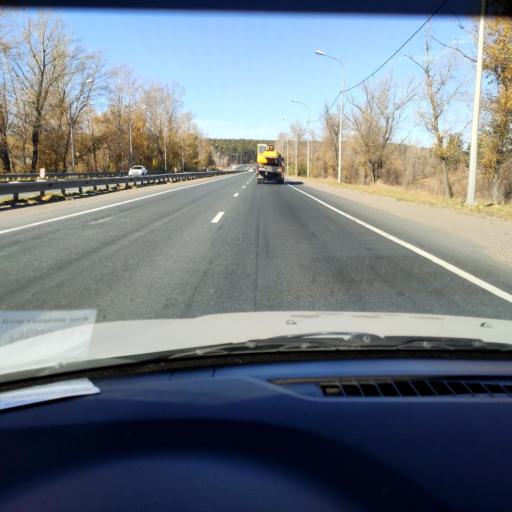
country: RU
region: Samara
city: Zhigulevsk
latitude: 53.5283
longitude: 49.5223
